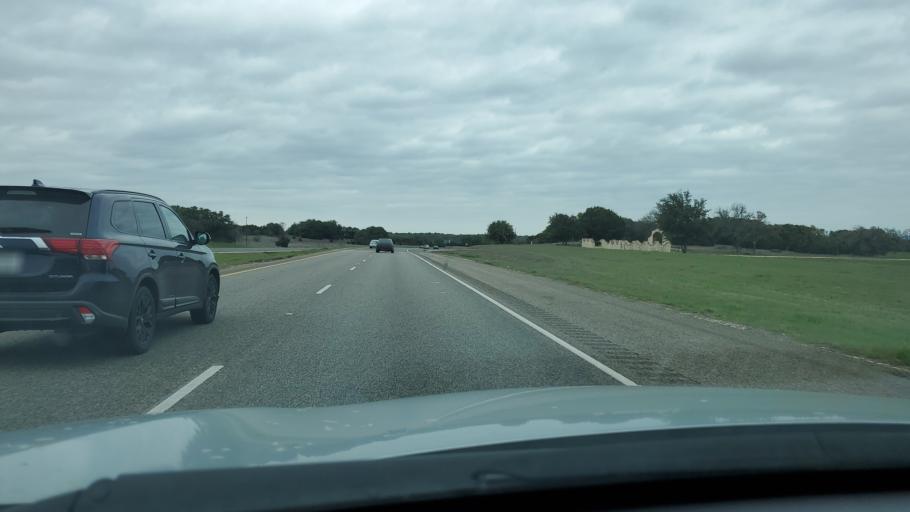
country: US
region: Texas
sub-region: Williamson County
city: Florence
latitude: 30.9012
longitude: -97.8006
